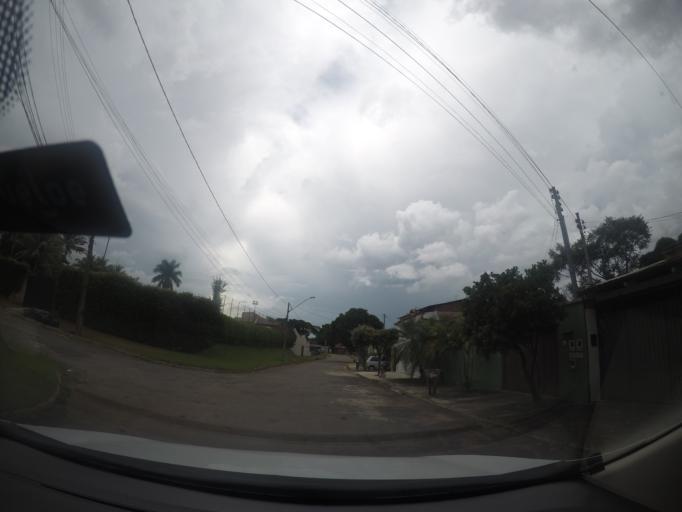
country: BR
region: Goias
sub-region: Goiania
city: Goiania
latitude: -16.6498
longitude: -49.2385
